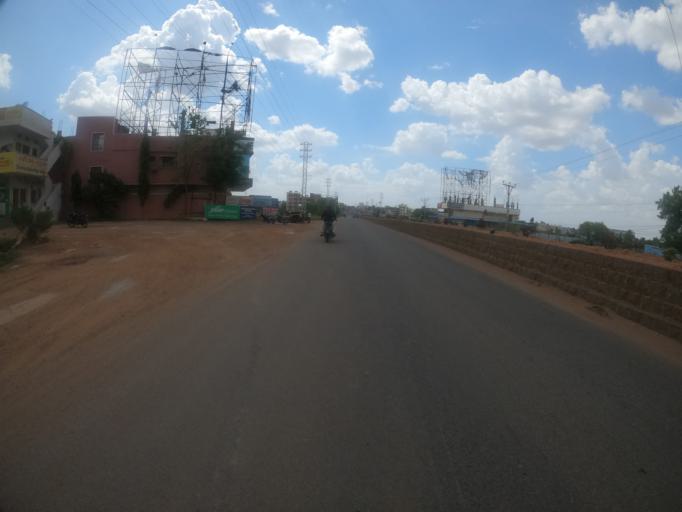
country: IN
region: Telangana
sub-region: Rangareddi
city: Sriramnagar
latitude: 17.3063
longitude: 78.1448
